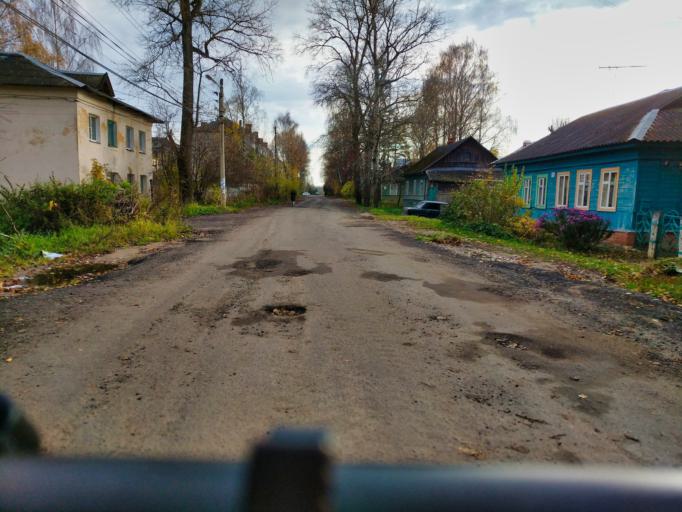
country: RU
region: Tverskaya
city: Rzhev
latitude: 56.2667
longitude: 34.3259
